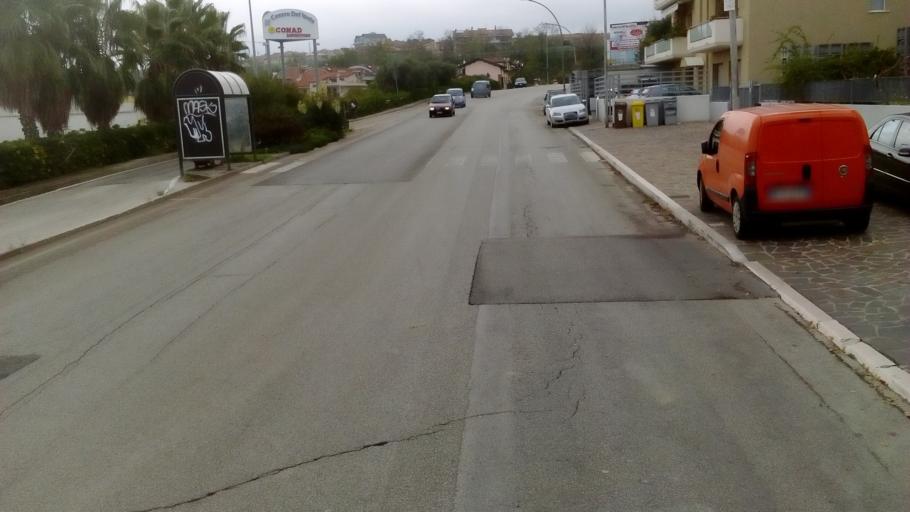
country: IT
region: Abruzzo
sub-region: Provincia di Chieti
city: Vasto
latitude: 42.0998
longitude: 14.7009
